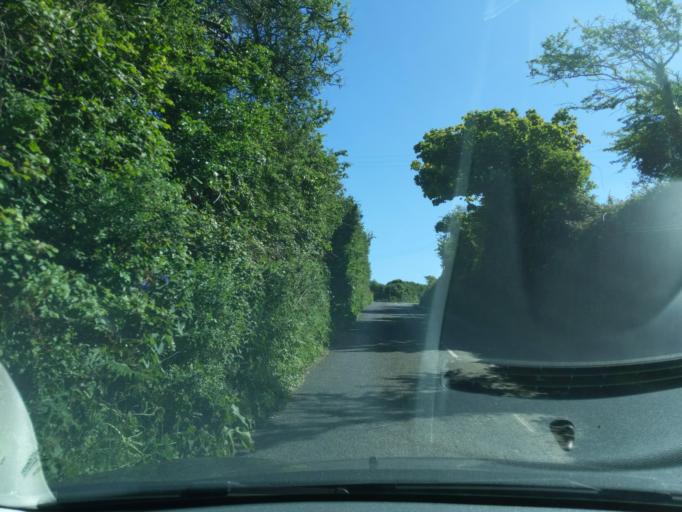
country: GB
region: England
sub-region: Cornwall
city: St. Buryan
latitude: 50.0953
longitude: -5.5949
